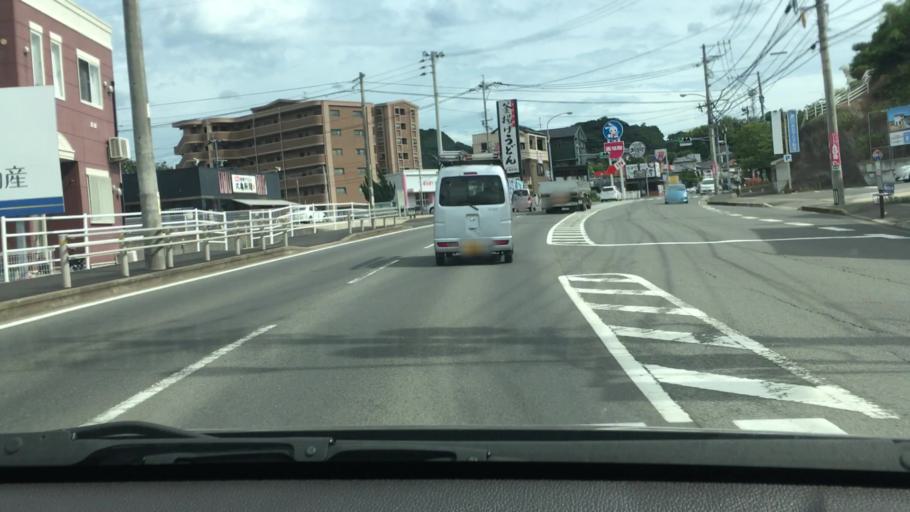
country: JP
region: Nagasaki
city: Togitsu
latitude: 32.8400
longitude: 129.8376
